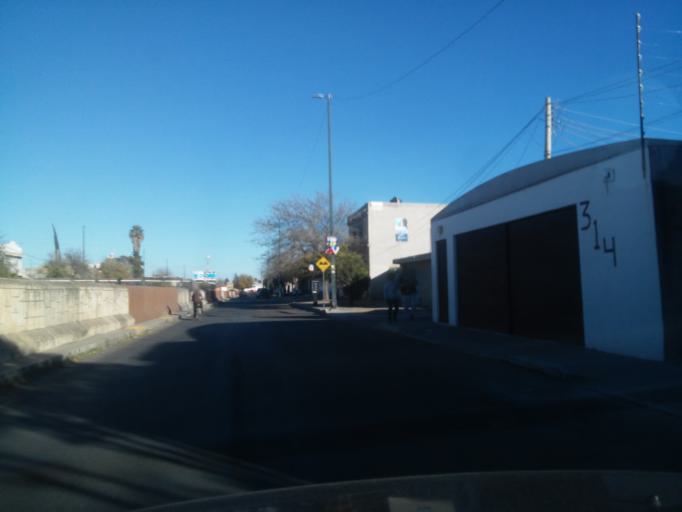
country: MX
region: Durango
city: Victoria de Durango
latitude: 24.0156
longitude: -104.6415
